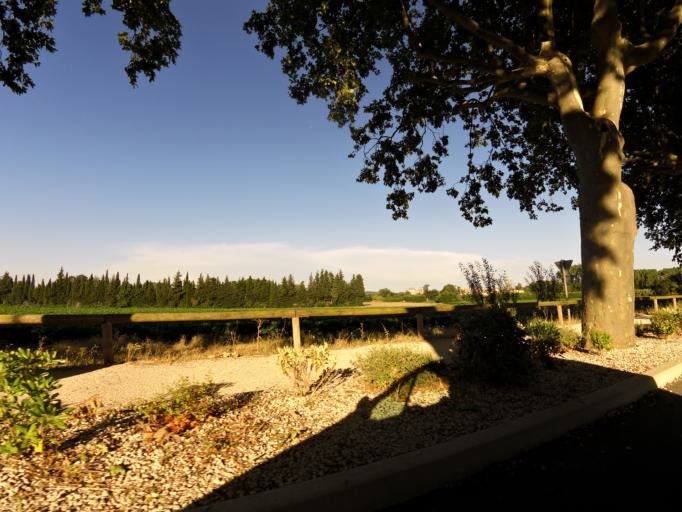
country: FR
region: Languedoc-Roussillon
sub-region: Departement du Gard
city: Remoulins
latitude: 43.9423
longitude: 4.5517
